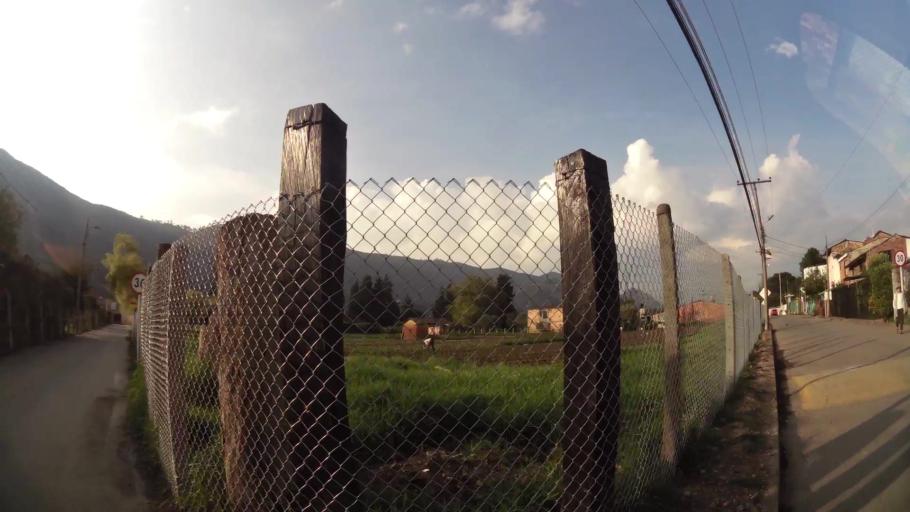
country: CO
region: Cundinamarca
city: Cota
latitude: 4.8134
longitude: -74.1044
